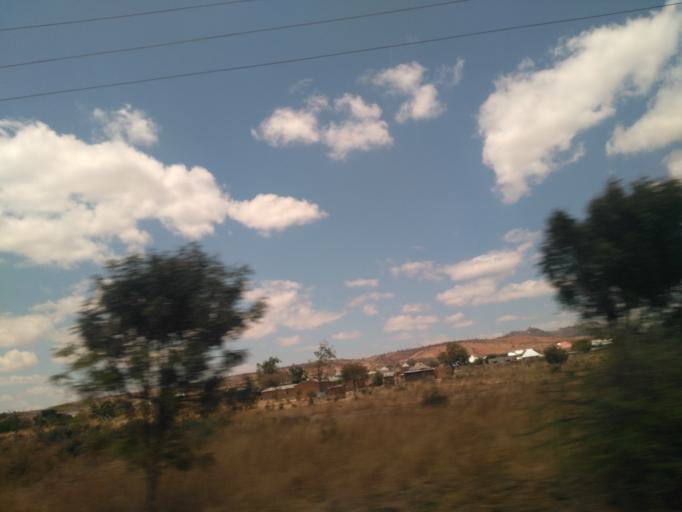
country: TZ
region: Dodoma
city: Kisasa
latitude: -6.1805
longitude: 35.7973
